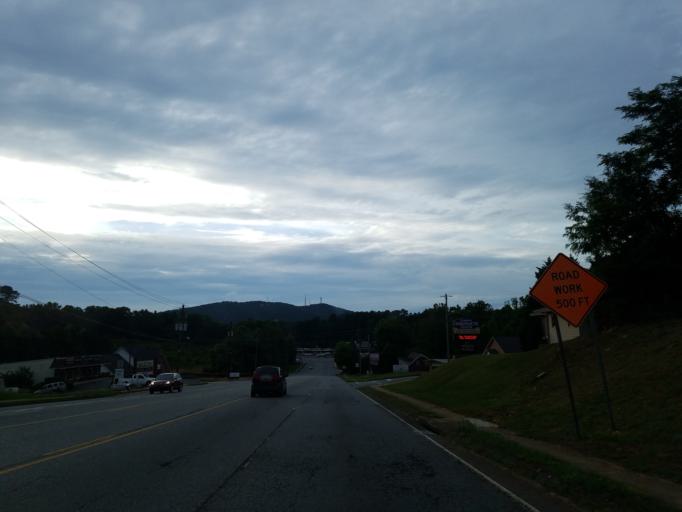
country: US
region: Georgia
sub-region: Forsyth County
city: Cumming
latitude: 34.2088
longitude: -84.1431
